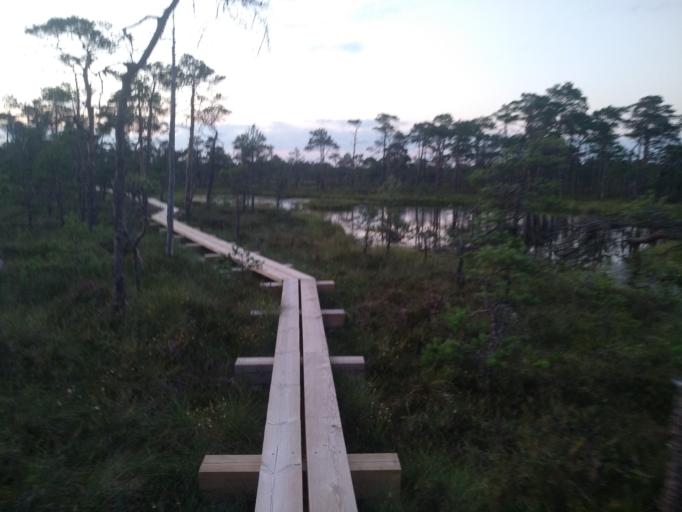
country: EE
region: Jaervamaa
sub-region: Paide linn
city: Paide
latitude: 59.0751
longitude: 25.5238
